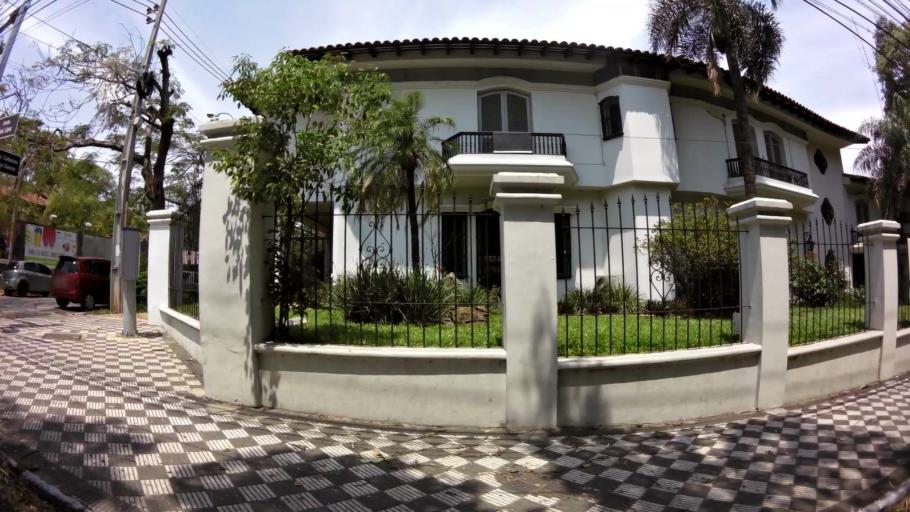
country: PY
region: Central
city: Lambare
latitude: -25.2962
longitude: -57.5751
